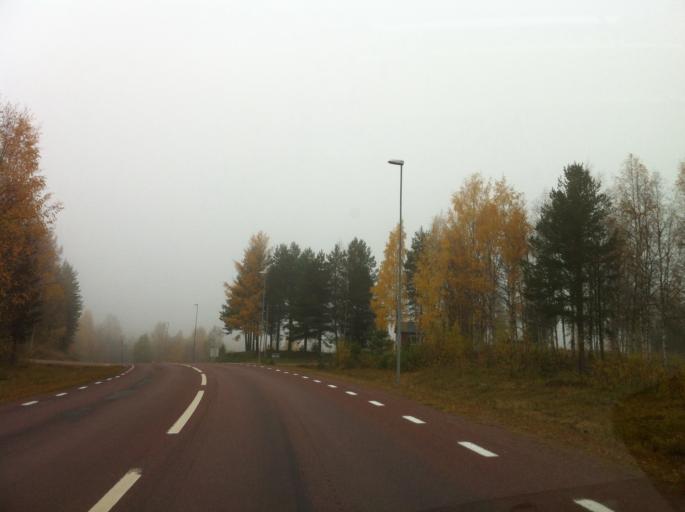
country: NO
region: Hedmark
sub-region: Trysil
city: Innbygda
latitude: 61.6897
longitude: 13.1603
